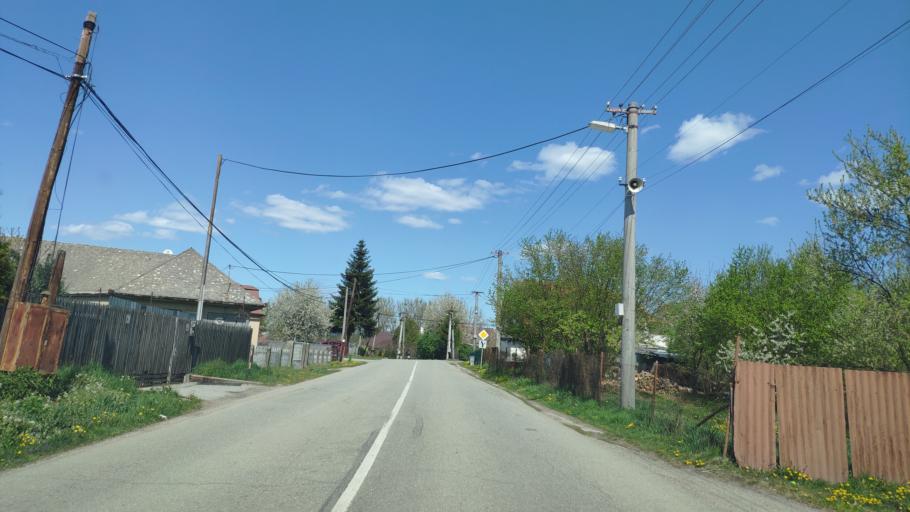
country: SK
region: Kosicky
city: Kosice
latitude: 48.6676
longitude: 21.4135
